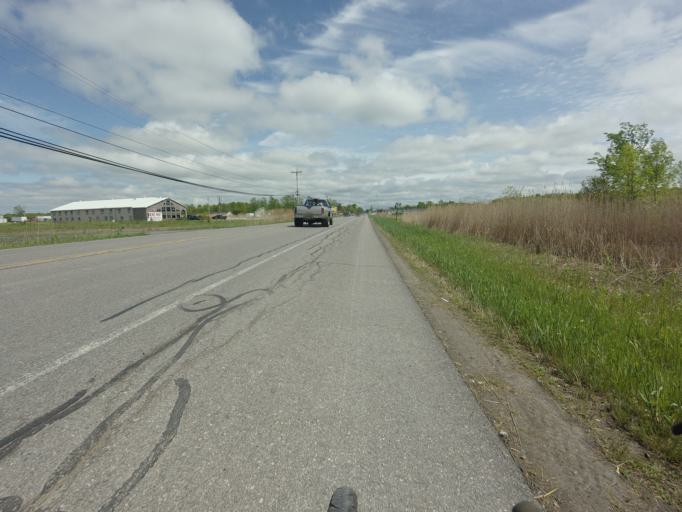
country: CA
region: Ontario
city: Cornwall
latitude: 44.9782
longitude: -74.6816
